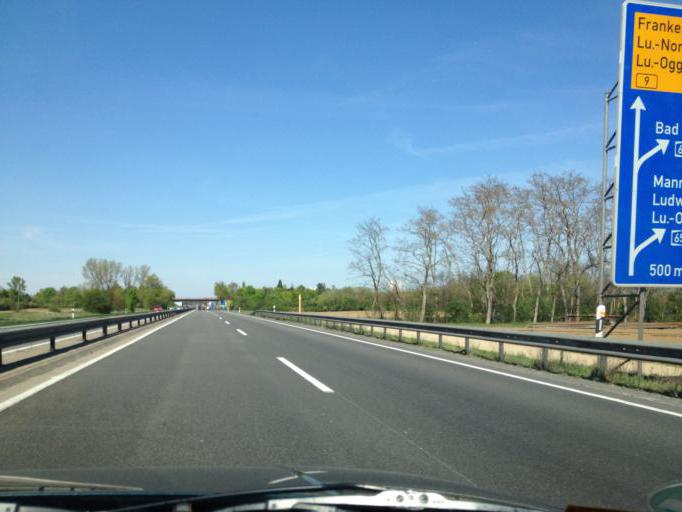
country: DE
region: Rheinland-Pfalz
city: Mutterstadt
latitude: 49.4740
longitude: 8.3600
